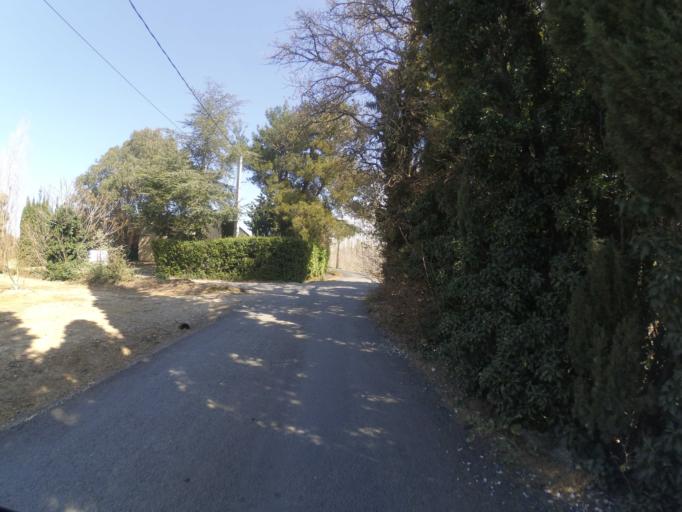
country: FR
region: Languedoc-Roussillon
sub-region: Departement des Pyrenees-Orientales
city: Pezilla-la-Riviere
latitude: 42.6718
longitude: 2.7619
